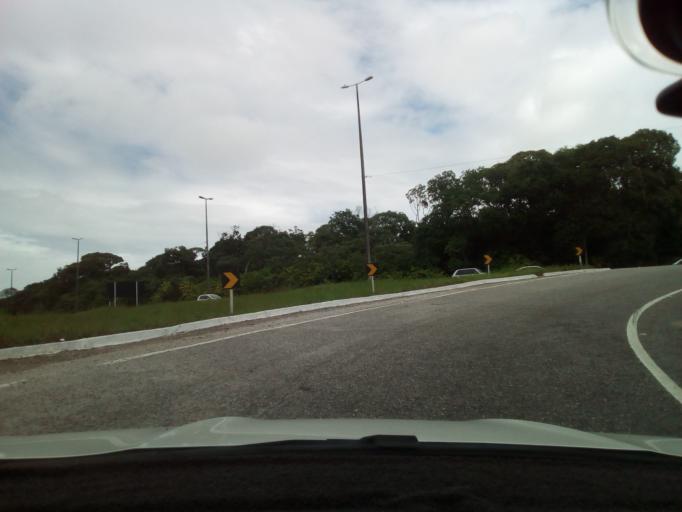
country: BR
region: Paraiba
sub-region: Joao Pessoa
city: Joao Pessoa
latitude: -7.1383
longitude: -34.8524
